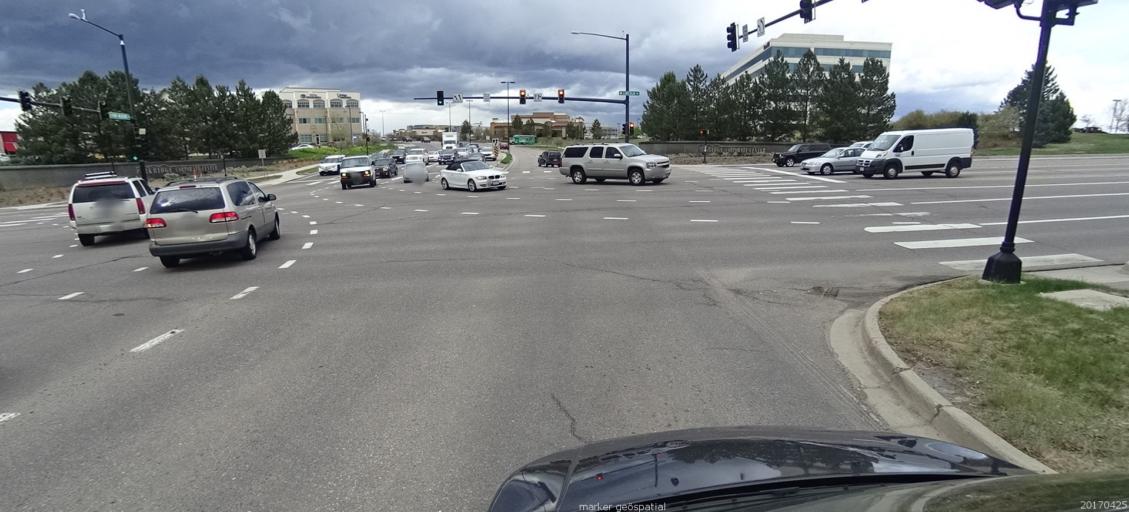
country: US
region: Colorado
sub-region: Adams County
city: Lone Tree
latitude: 39.5360
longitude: -104.8729
